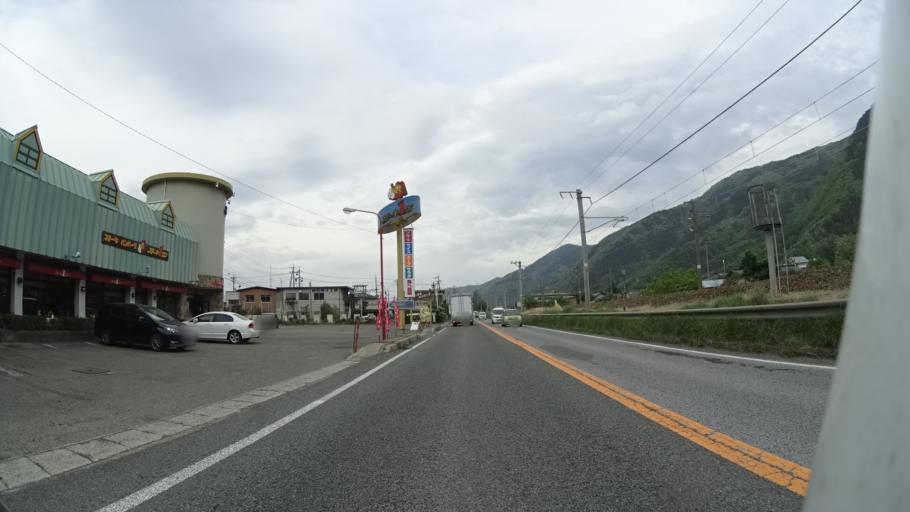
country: JP
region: Nagano
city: Ueda
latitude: 36.4760
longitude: 138.1584
